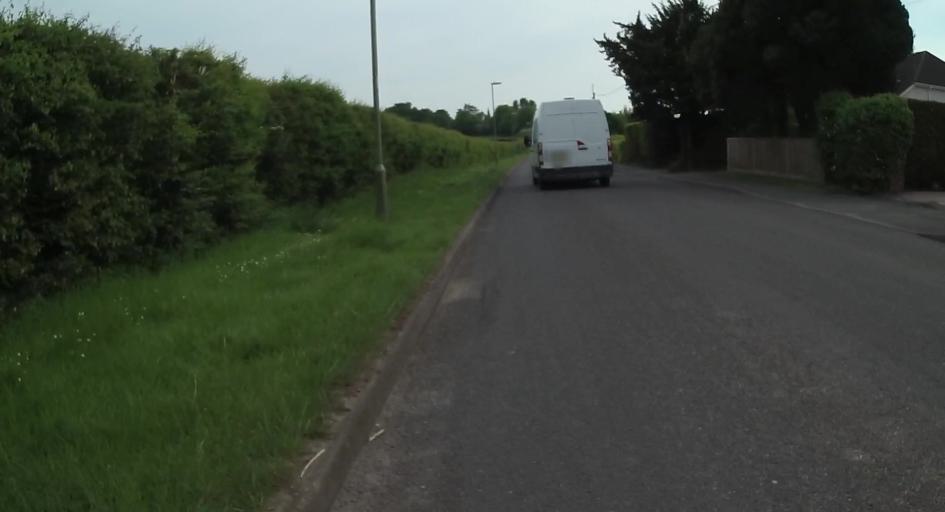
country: GB
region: England
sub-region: Hampshire
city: Basingstoke
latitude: 51.2569
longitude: -1.1686
